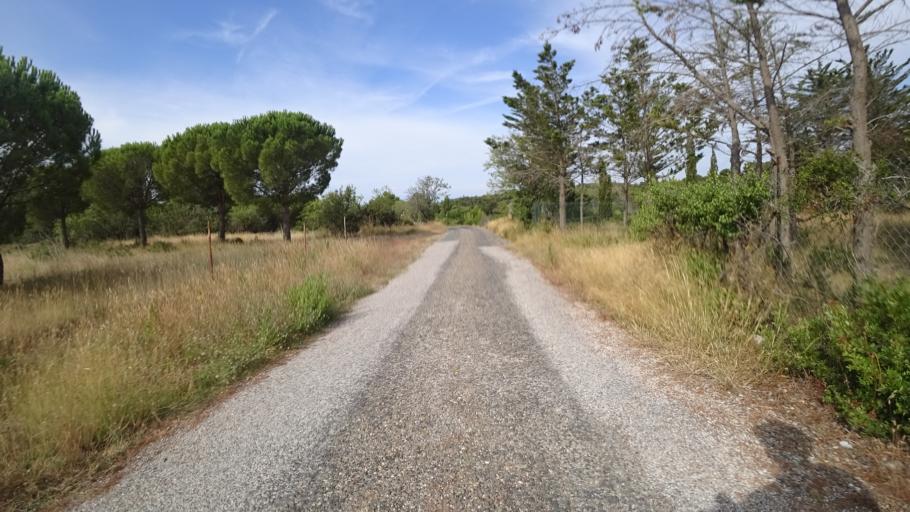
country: FR
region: Languedoc-Roussillon
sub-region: Departement de l'Aude
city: Leucate
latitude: 42.9000
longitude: 3.0298
